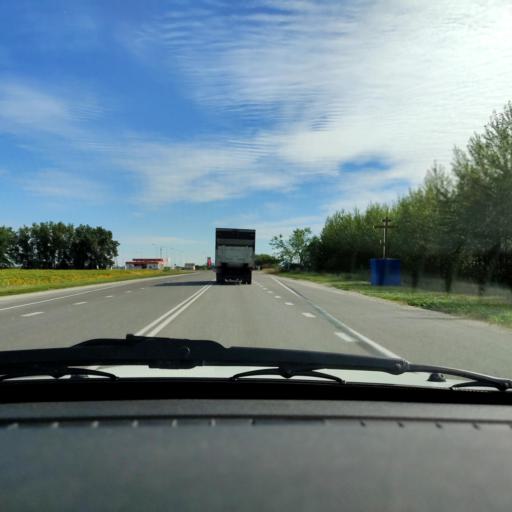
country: RU
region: Voronezj
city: Orlovo
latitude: 51.7337
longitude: 39.5621
